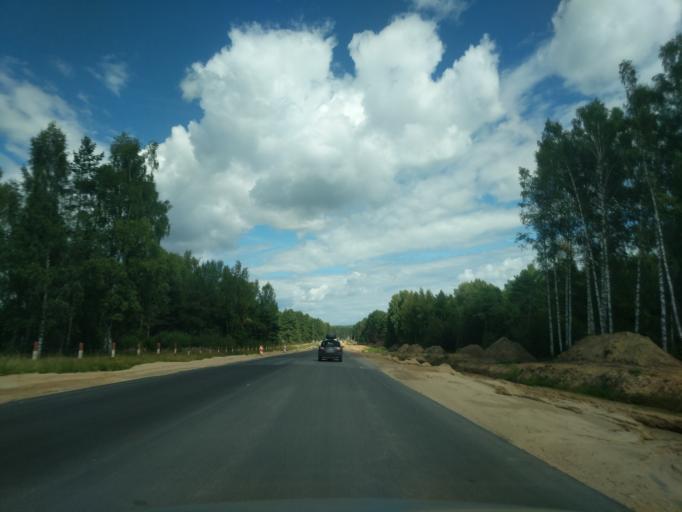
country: RU
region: Jaroslavl
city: Levashevo
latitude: 57.6639
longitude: 40.5724
